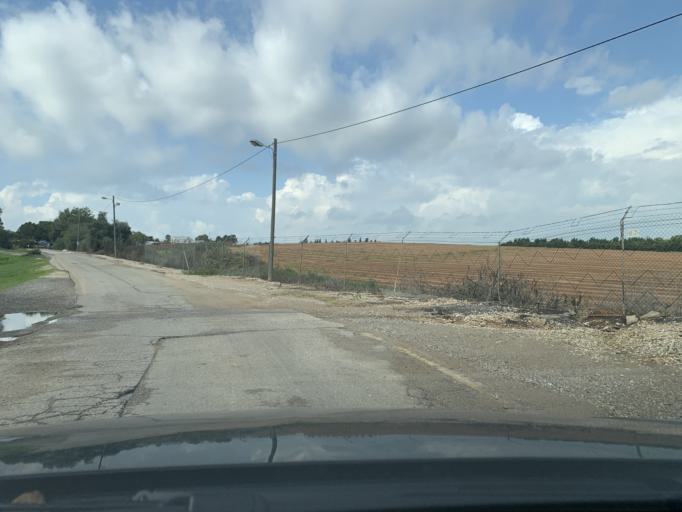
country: PS
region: West Bank
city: Qalqilyah
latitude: 32.1969
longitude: 34.9534
